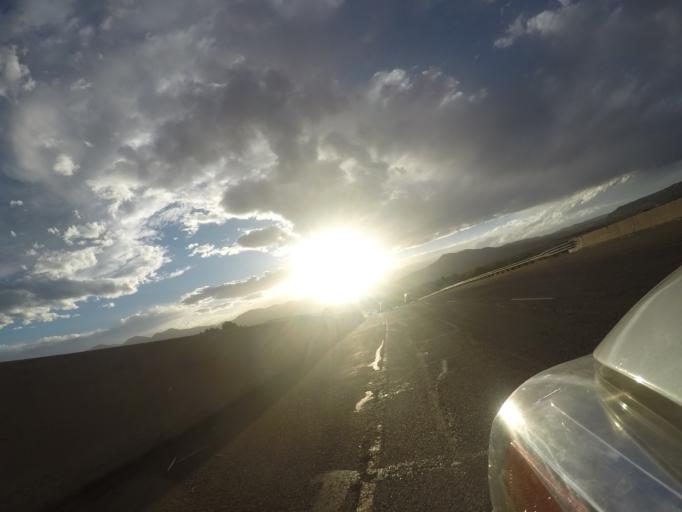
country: US
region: Colorado
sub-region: Jefferson County
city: Lakewood
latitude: 39.6539
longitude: -105.1097
